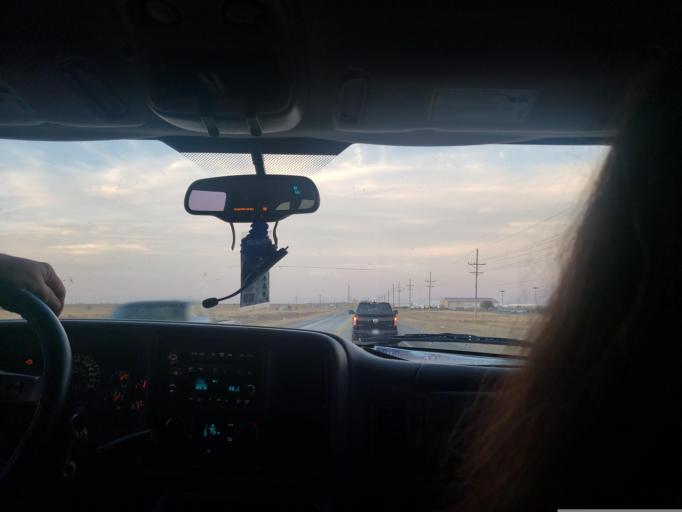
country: US
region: Kansas
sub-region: Seward County
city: Liberal
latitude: 37.0625
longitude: -100.9044
